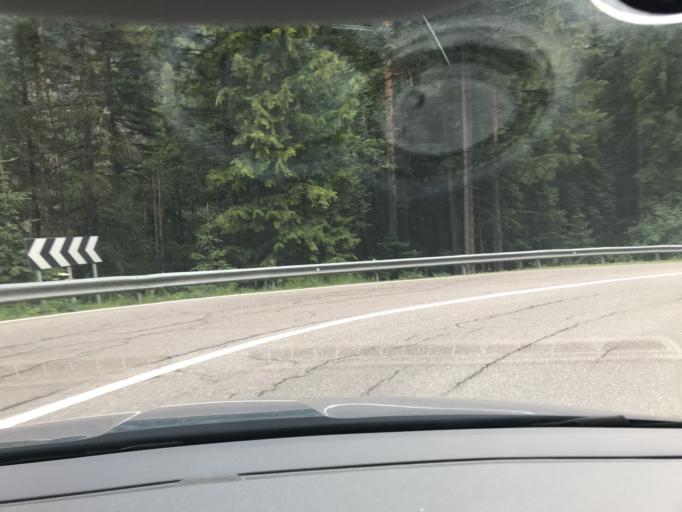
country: IT
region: Trentino-Alto Adige
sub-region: Bolzano
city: Badia
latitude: 46.6200
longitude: 11.8931
